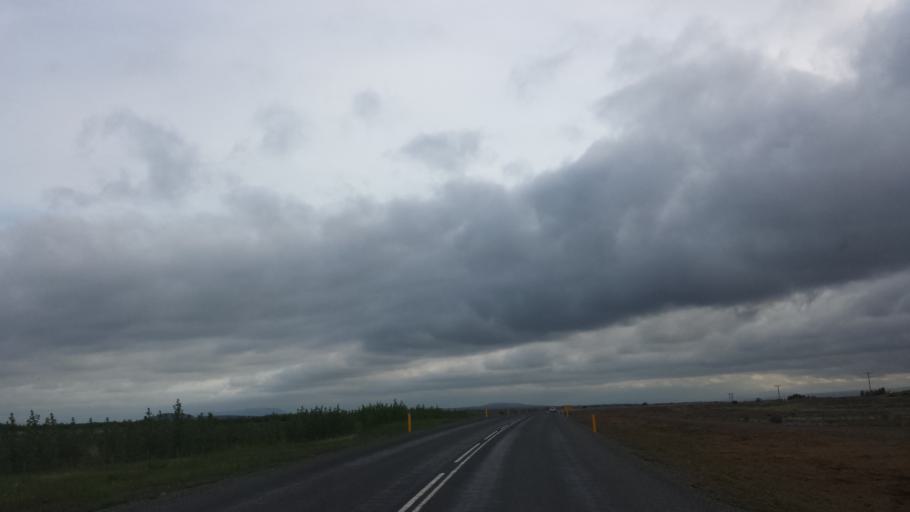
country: IS
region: South
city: Selfoss
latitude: 64.2761
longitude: -20.3509
